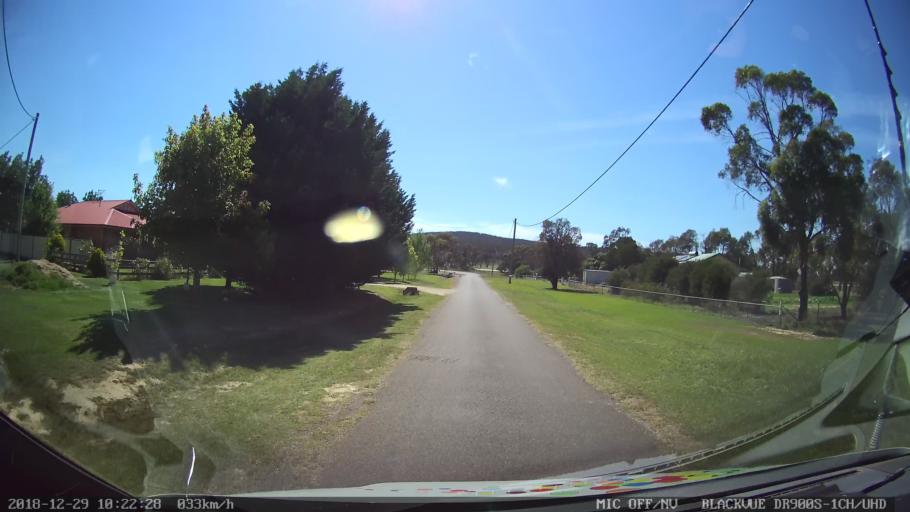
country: AU
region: New South Wales
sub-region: Yass Valley
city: Gundaroo
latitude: -34.9165
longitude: 149.4354
